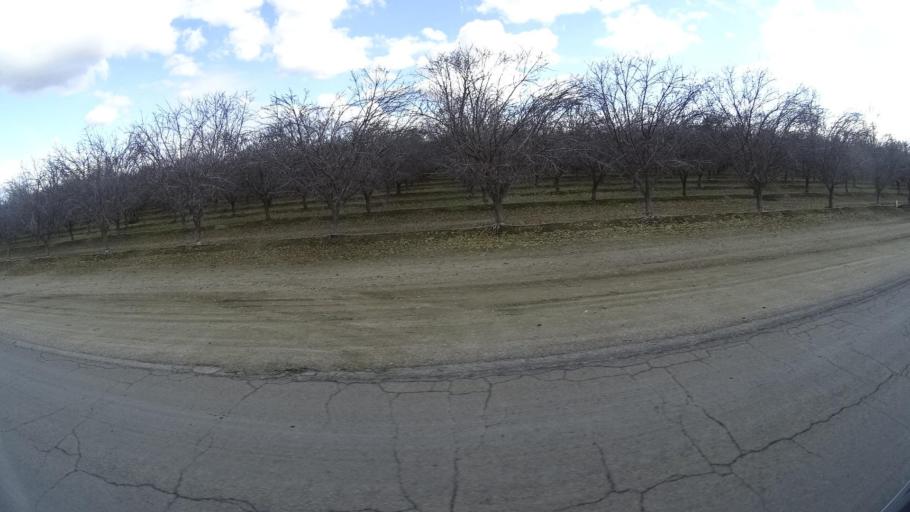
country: US
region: California
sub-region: Kern County
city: Greenfield
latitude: 35.2143
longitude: -119.0923
